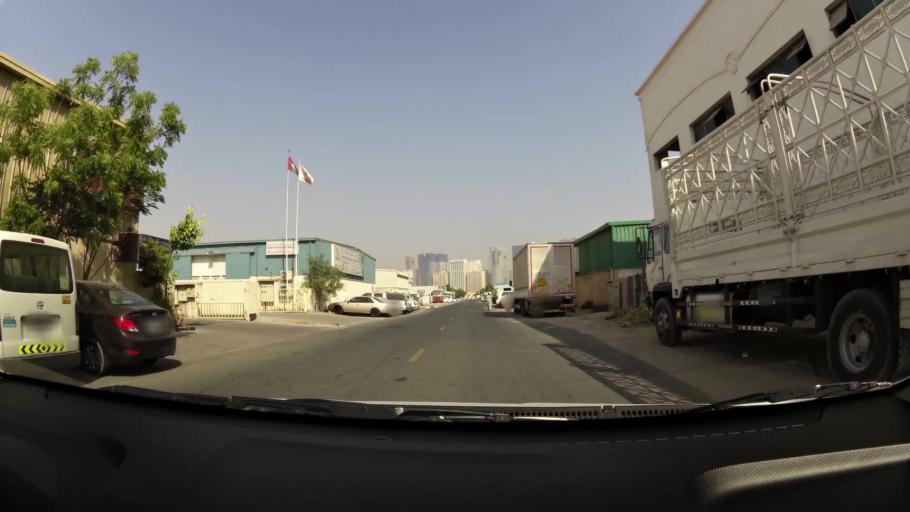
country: AE
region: Ash Shariqah
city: Sharjah
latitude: 25.2955
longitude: 55.3947
